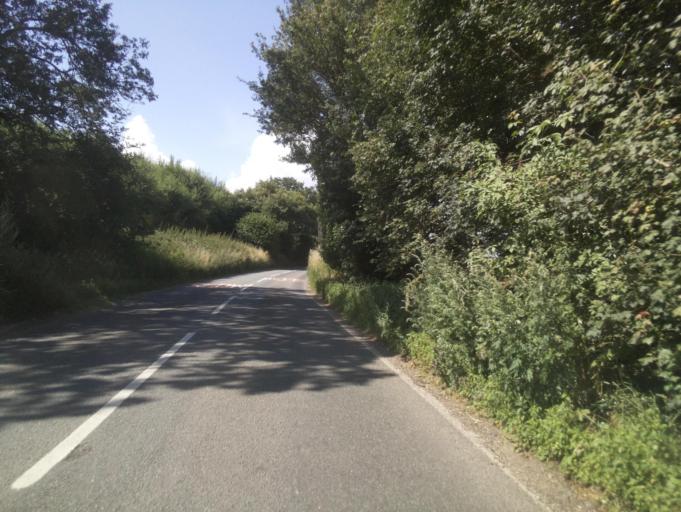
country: GB
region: England
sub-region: West Berkshire
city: Winterbourne
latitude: 51.4728
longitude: -1.3566
